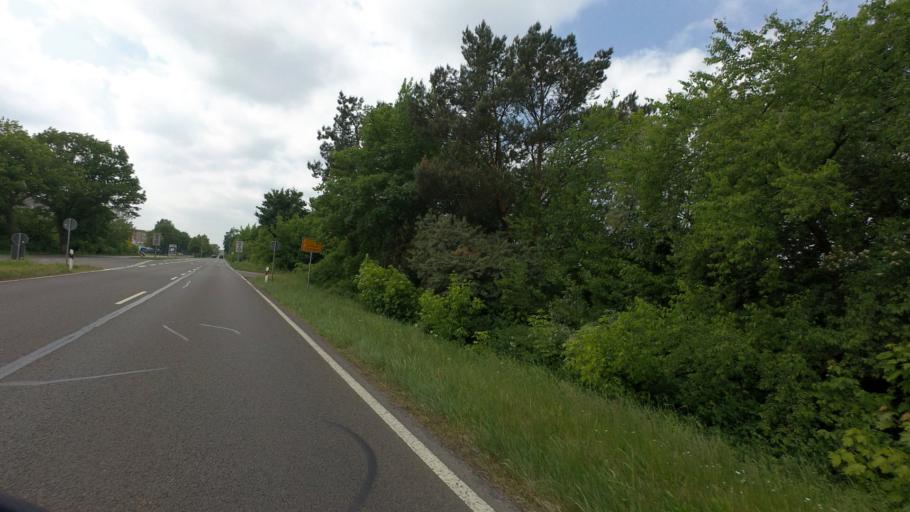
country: DE
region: Brandenburg
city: Cottbus
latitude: 51.7785
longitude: 14.3665
